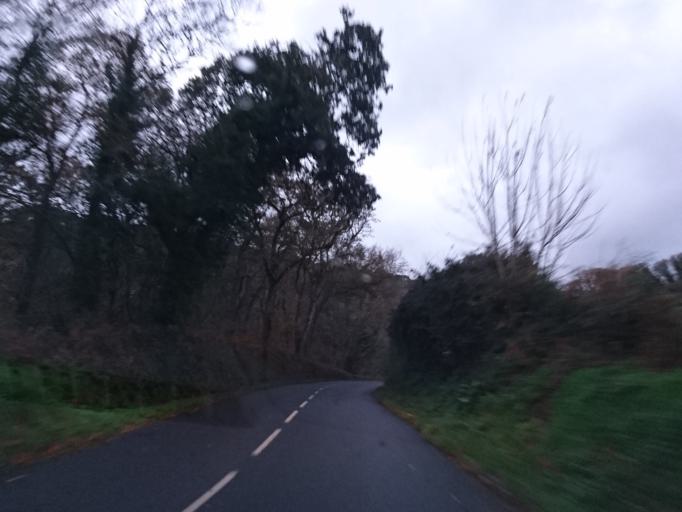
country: FR
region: Brittany
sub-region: Departement du Finistere
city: Le Conquet
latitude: 48.3658
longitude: -4.7457
